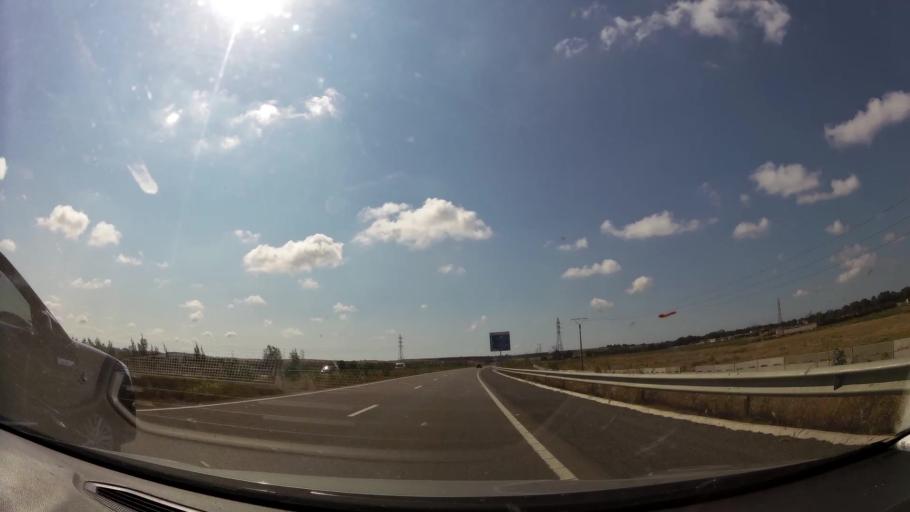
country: MA
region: Rabat-Sale-Zemmour-Zaer
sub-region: Skhirate-Temara
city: Temara
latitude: 33.8403
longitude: -6.8843
